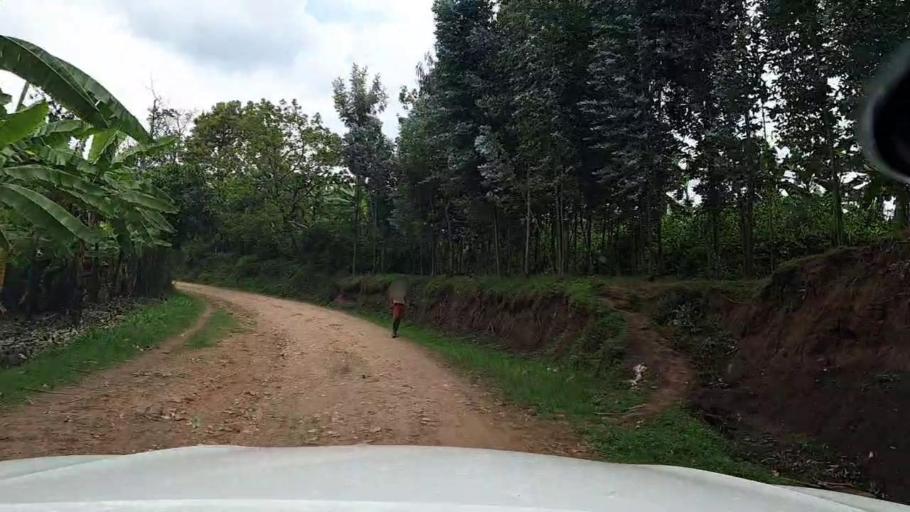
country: RW
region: Western Province
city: Kibuye
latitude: -2.0755
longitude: 29.4236
